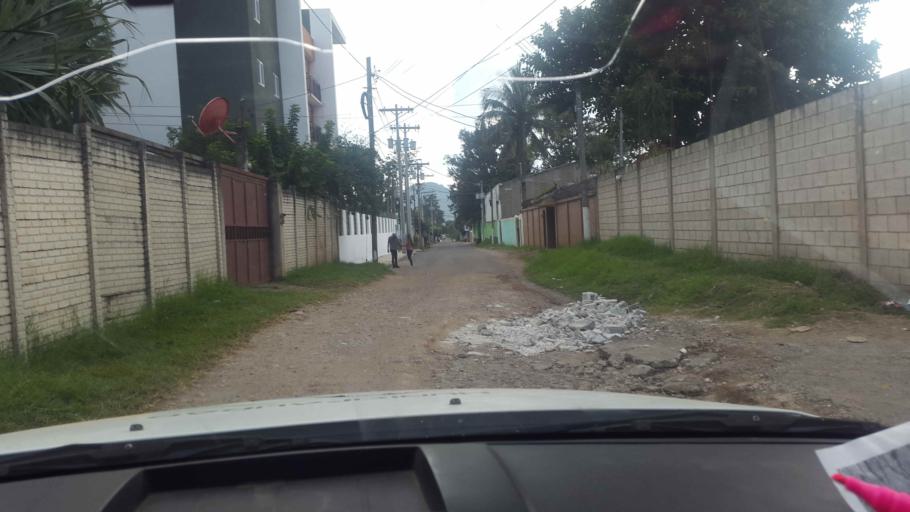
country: GT
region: Guatemala
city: Petapa
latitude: 14.5172
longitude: -90.5385
